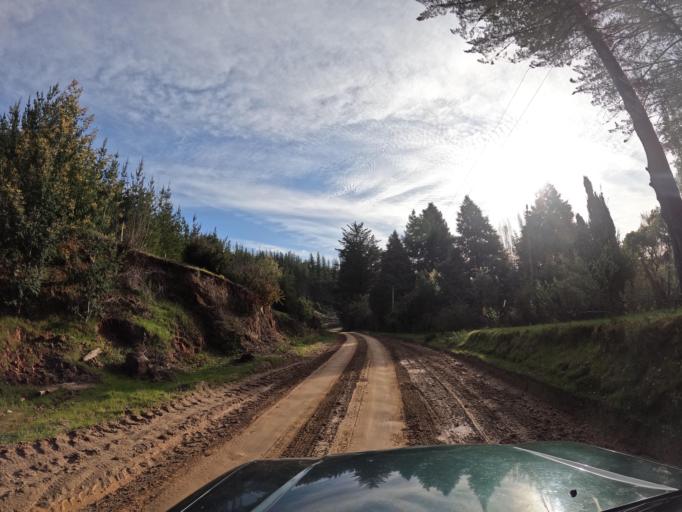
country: CL
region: Biobio
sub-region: Provincia de Biobio
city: La Laja
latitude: -37.1952
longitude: -72.7525
